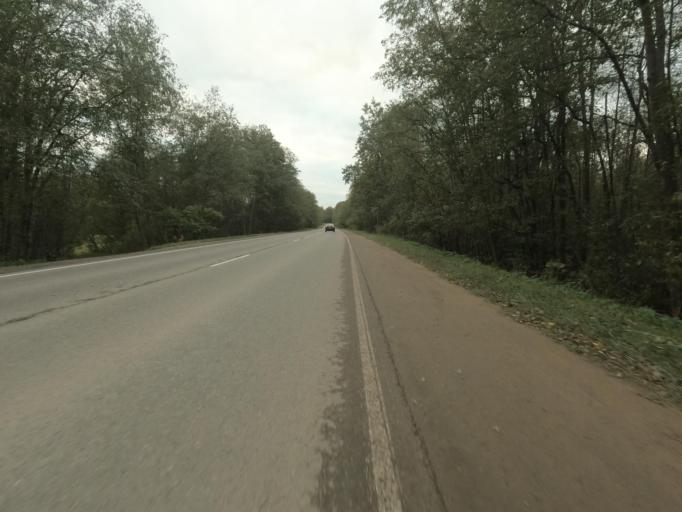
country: RU
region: Leningrad
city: Pavlovo
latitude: 59.7946
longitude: 30.9530
